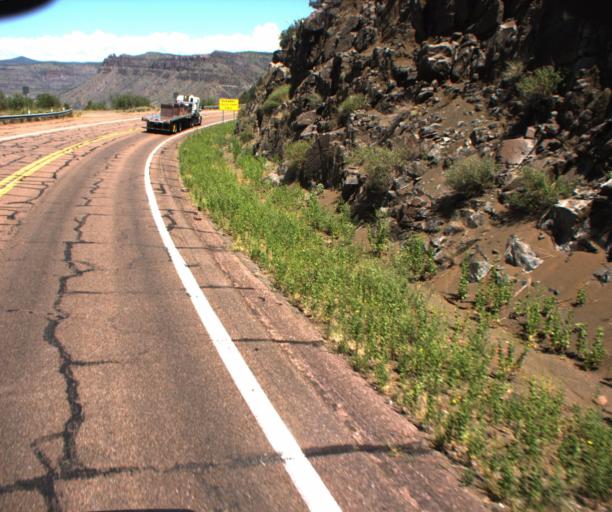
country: US
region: Arizona
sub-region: Navajo County
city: Cibecue
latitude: 33.7871
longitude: -110.5033
